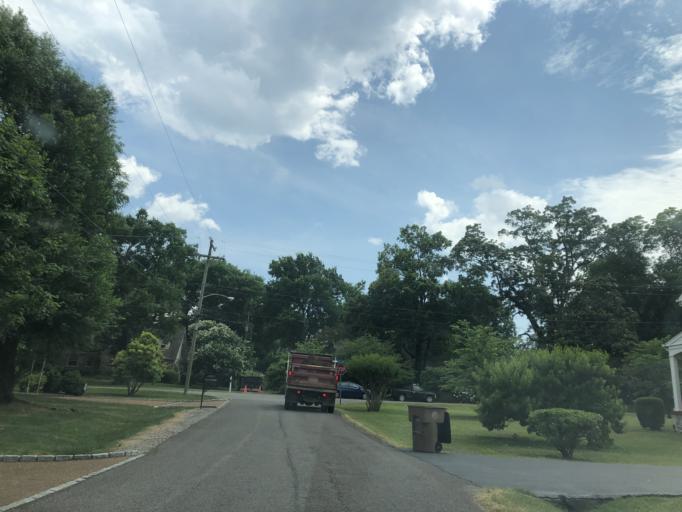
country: US
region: Tennessee
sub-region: Davidson County
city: Belle Meade
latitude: 36.1209
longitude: -86.8191
